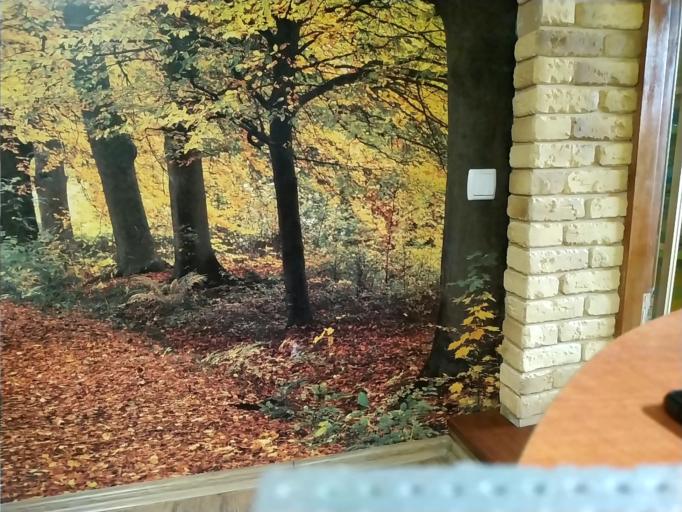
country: RU
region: Vladimir
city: Bavleny
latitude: 56.3673
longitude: 39.5607
